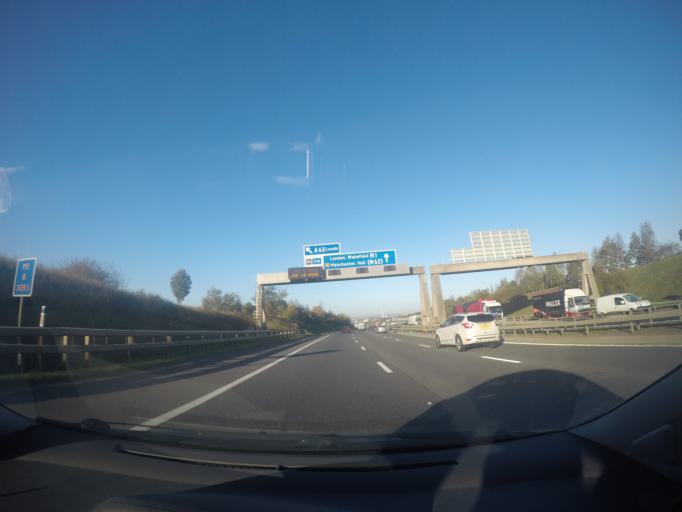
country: GB
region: England
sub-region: City and Borough of Leeds
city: Swillington
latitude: 53.7741
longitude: -1.4454
